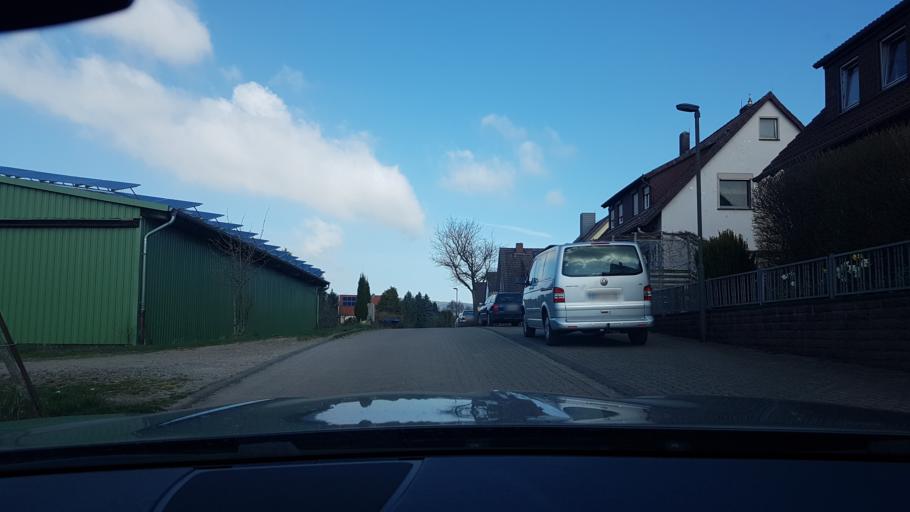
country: DE
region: Lower Saxony
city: Bad Munder am Deister
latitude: 52.1285
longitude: 9.4476
